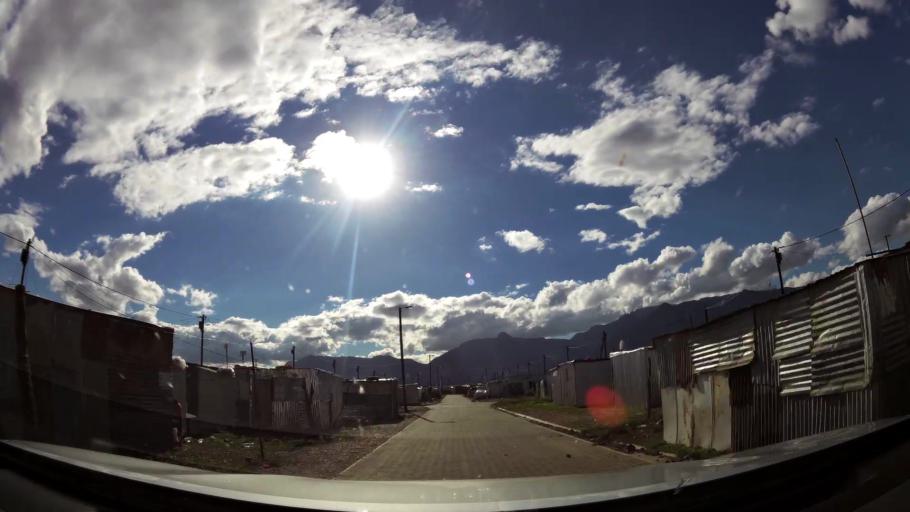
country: ZA
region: Western Cape
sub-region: Overberg District Municipality
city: Swellendam
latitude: -34.0489
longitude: 20.4394
